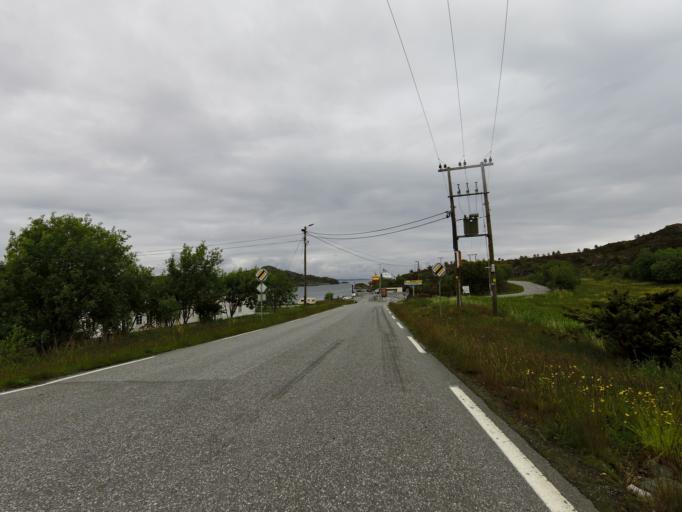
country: NO
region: Hordaland
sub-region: Sveio
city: Sveio
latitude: 59.6065
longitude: 5.2342
